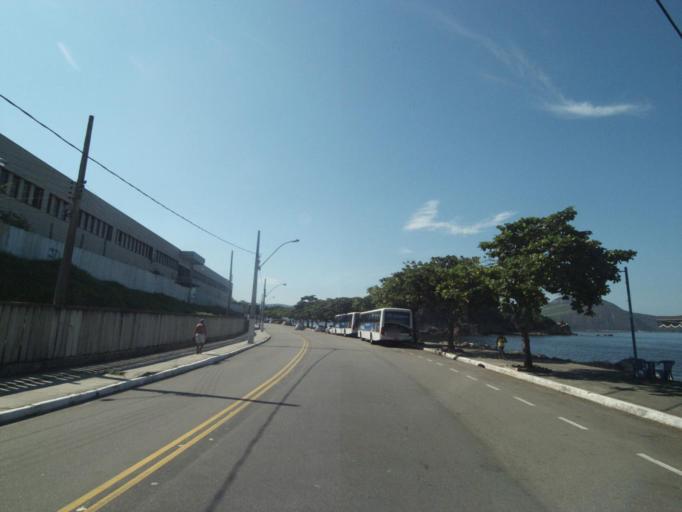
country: BR
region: Rio de Janeiro
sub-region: Niteroi
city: Niteroi
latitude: -22.9071
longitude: -43.1331
